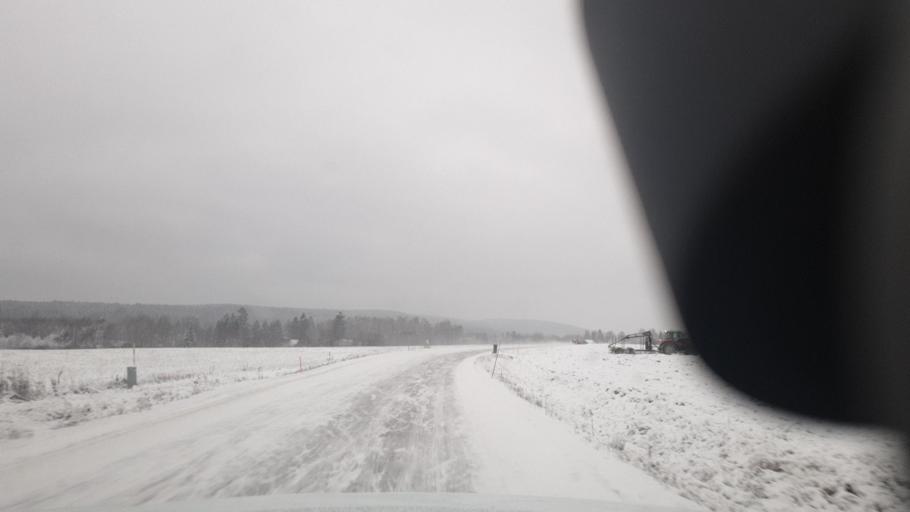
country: SE
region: Vaermland
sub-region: Eda Kommun
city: Charlottenberg
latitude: 59.7529
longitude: 12.1582
